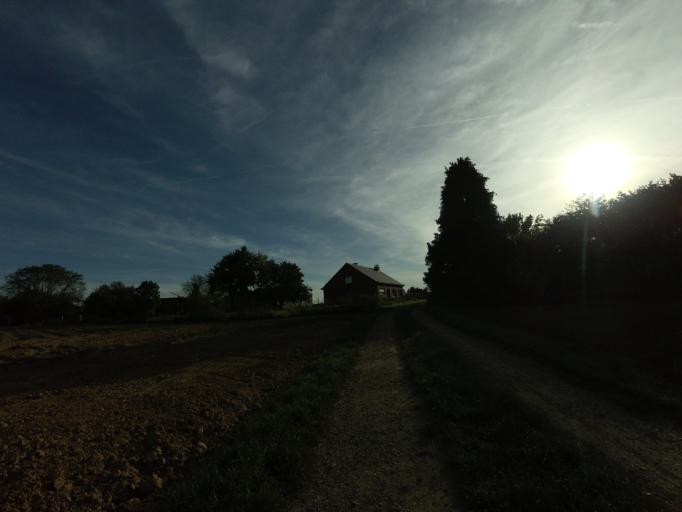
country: BE
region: Flanders
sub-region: Provincie Vlaams-Brabant
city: Bertem
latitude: 50.8965
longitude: 4.6055
